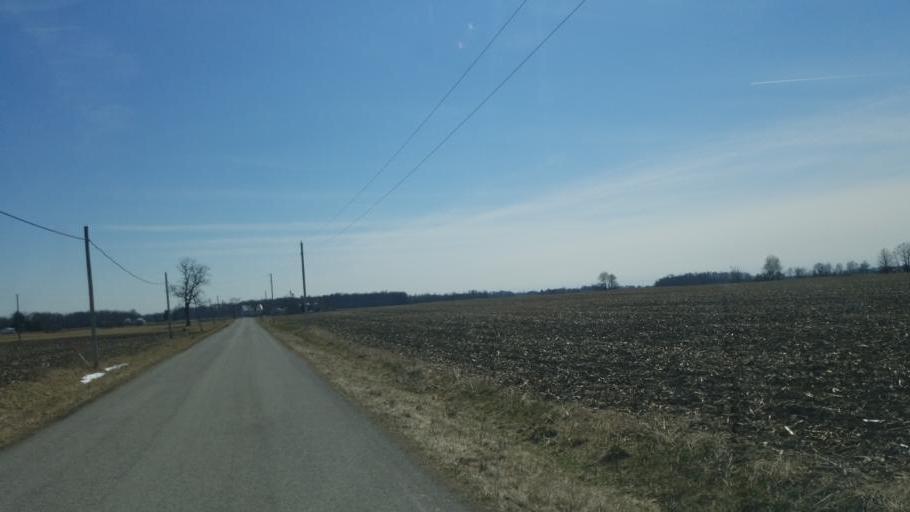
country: US
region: Ohio
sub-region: Crawford County
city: Bucyrus
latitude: 40.6723
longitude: -82.9695
